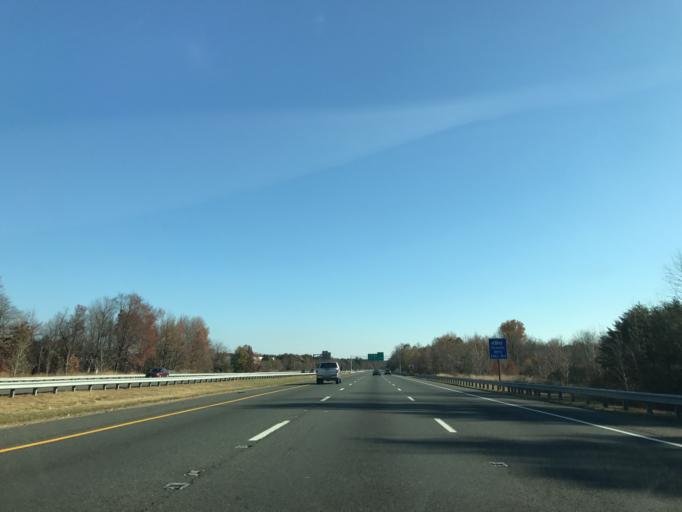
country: US
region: Maryland
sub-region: Anne Arundel County
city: Severn
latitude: 39.1553
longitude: -76.6668
